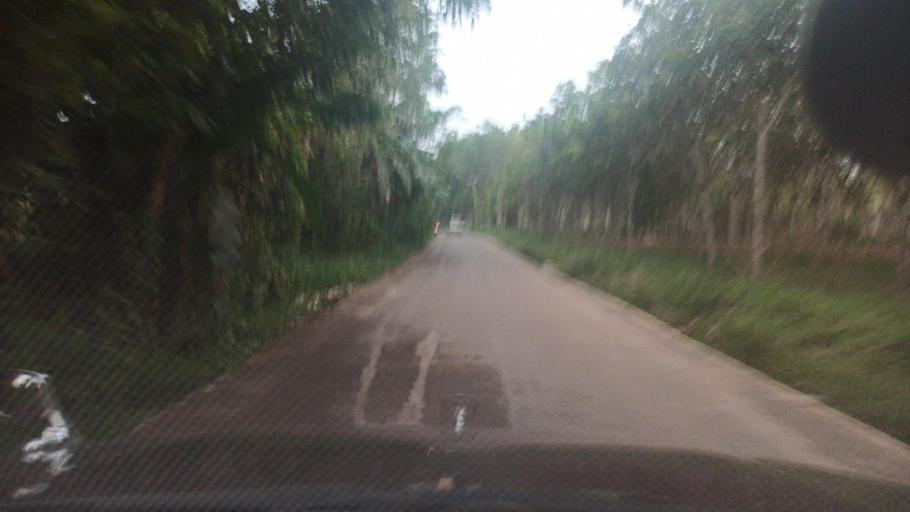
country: ID
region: South Sumatra
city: Gunungmenang
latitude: -3.2934
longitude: 104.1404
